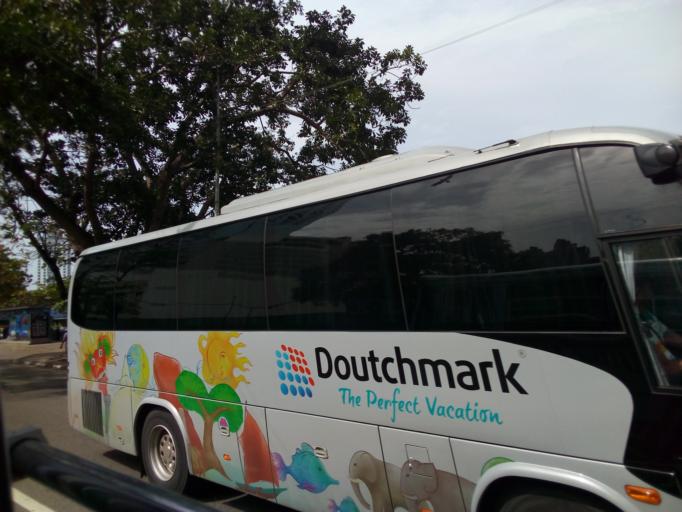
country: LK
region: Western
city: Colombo
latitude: 6.9184
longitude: 79.8543
